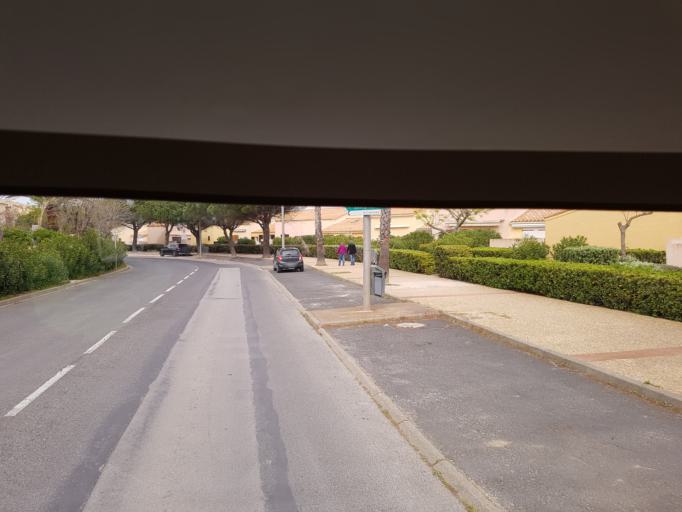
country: FR
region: Languedoc-Roussillon
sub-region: Departement de l'Aude
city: Fleury
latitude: 43.1840
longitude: 3.1958
